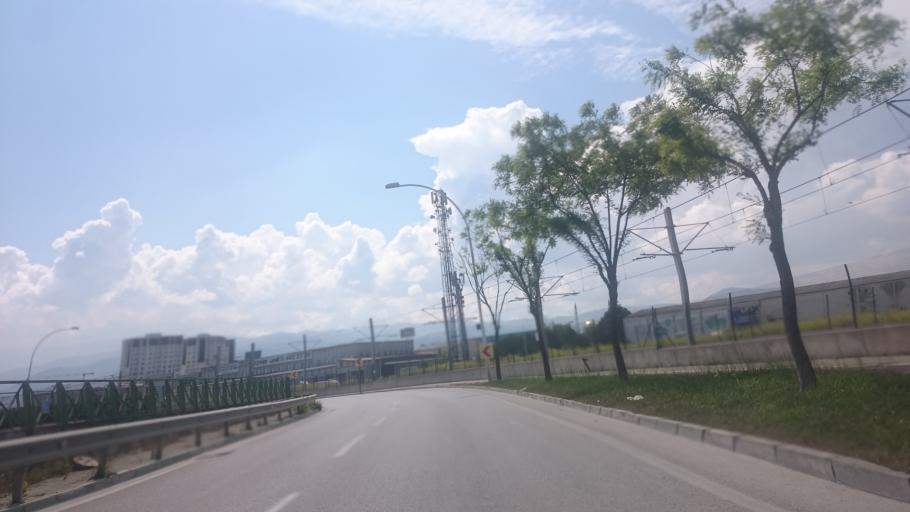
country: TR
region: Bursa
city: Cali
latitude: 40.2171
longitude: 28.9303
